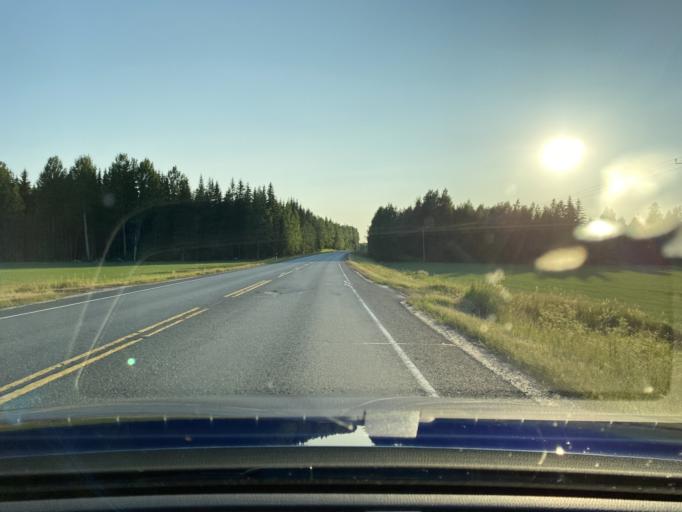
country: FI
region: Haeme
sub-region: Forssa
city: Tammela
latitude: 60.8268
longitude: 23.9046
